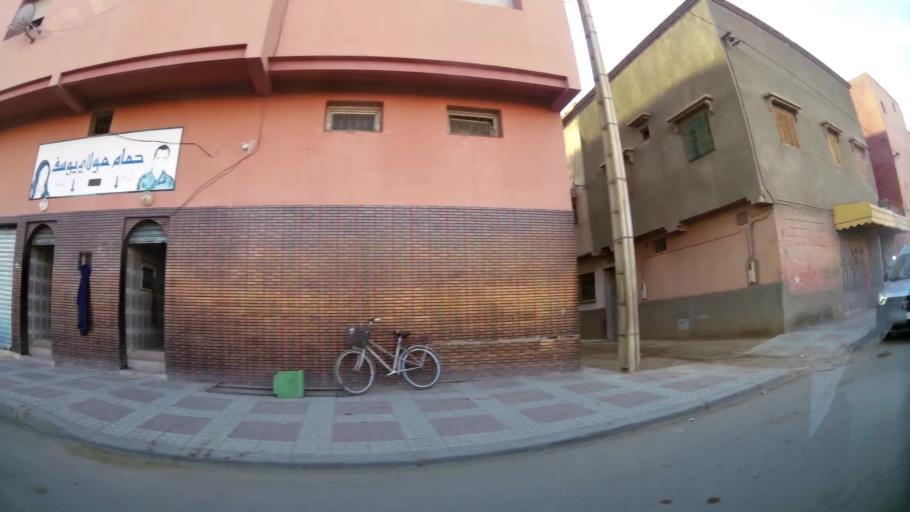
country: MA
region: Marrakech-Tensift-Al Haouz
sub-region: Kelaa-Des-Sraghna
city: Sidi Abdallah
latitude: 32.2406
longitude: -7.9500
